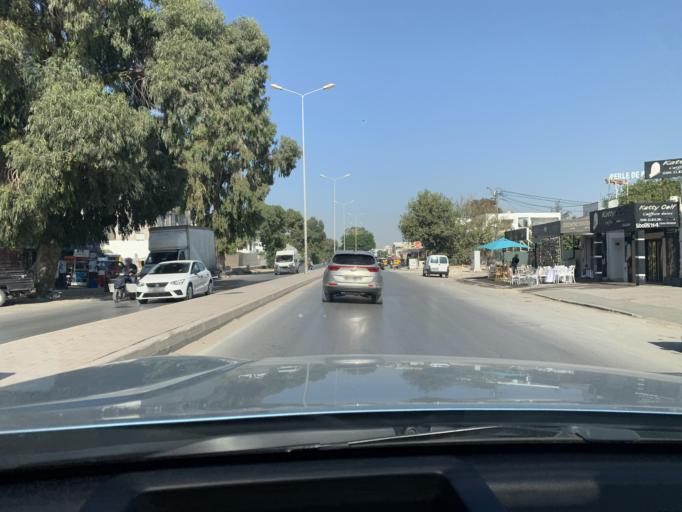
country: TN
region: Manouba
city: Manouba
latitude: 36.8190
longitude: 10.1249
